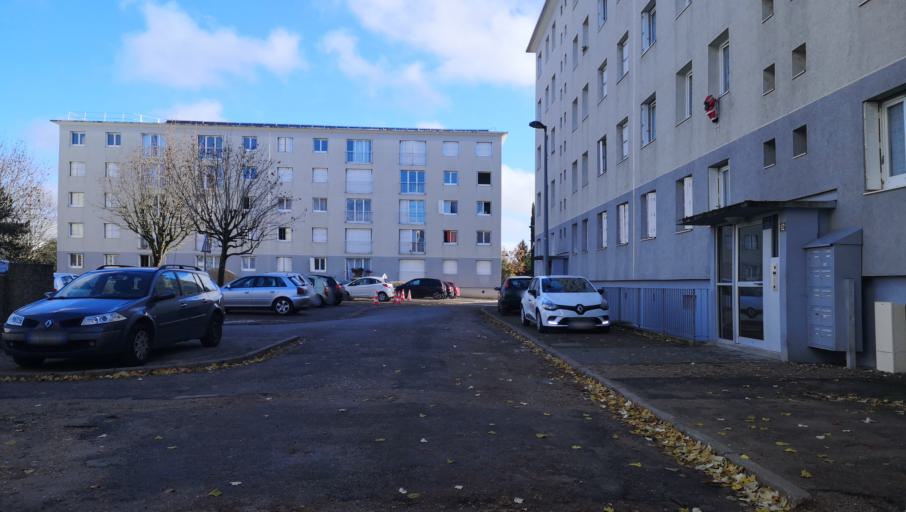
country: FR
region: Centre
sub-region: Departement du Loiret
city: Saint-Jean-le-Blanc
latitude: 47.9066
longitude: 1.9342
